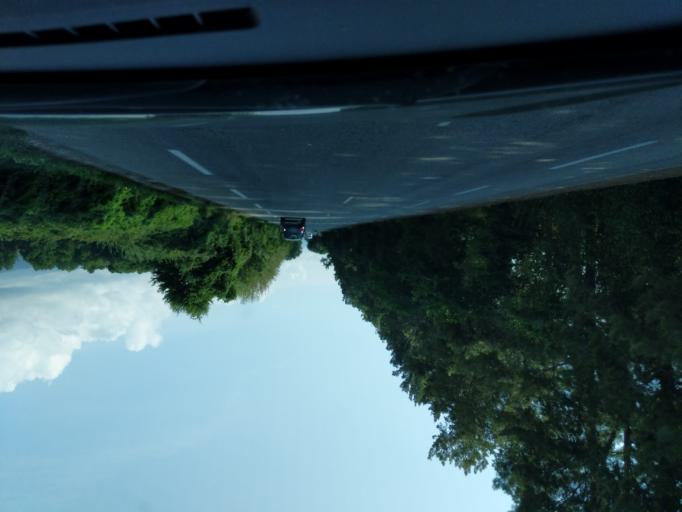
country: FR
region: Corsica
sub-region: Departement de la Haute-Corse
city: Ghisonaccia
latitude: 41.9709
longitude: 9.3986
